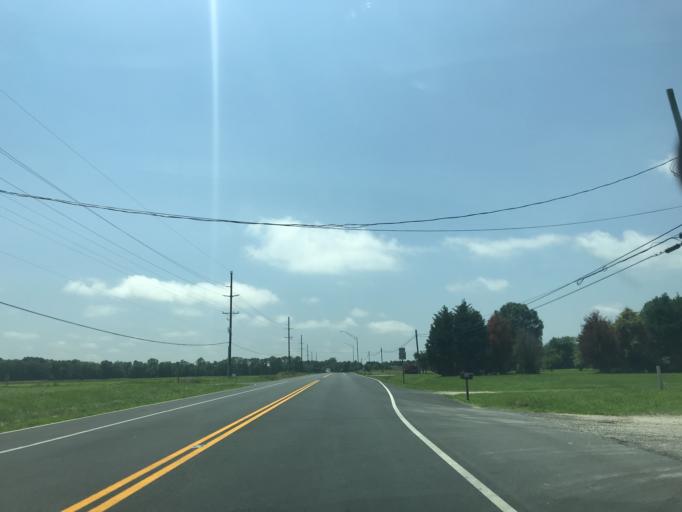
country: US
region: Maryland
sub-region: Dorchester County
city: Hurlock
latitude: 38.5916
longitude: -75.9477
